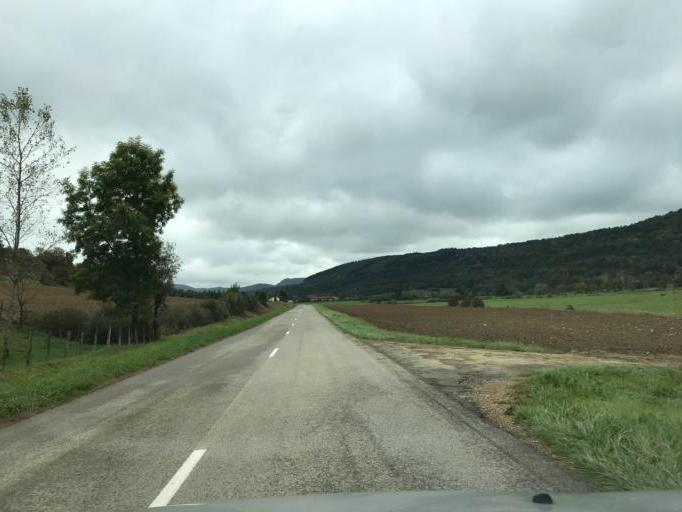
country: FR
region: Rhone-Alpes
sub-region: Departement de l'Ain
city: Coligny
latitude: 46.3817
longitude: 5.4436
